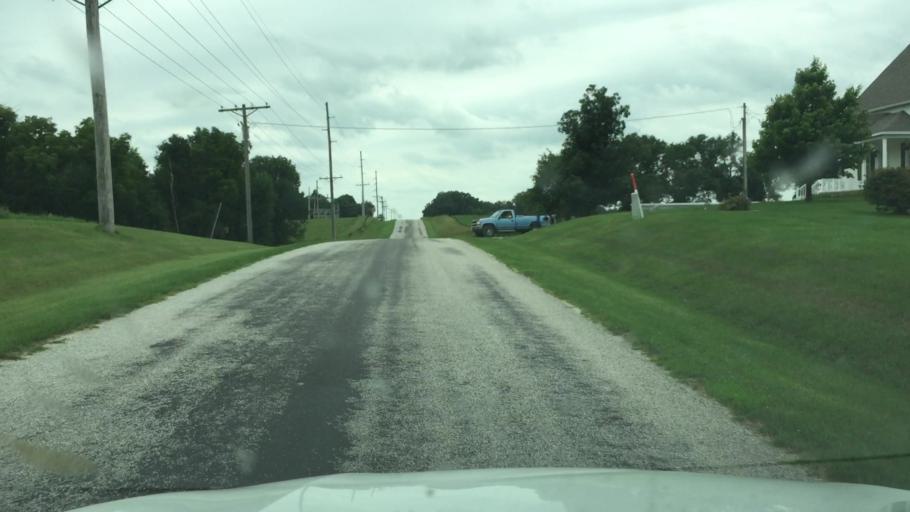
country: US
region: Illinois
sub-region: Hancock County
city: Carthage
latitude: 40.2985
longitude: -91.0832
